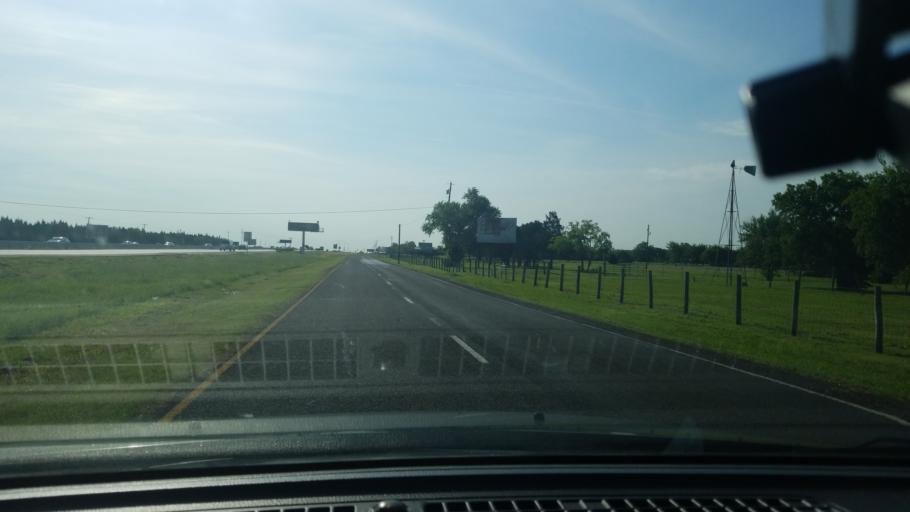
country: US
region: Texas
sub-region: Dallas County
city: Mesquite
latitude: 32.7887
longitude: -96.5866
